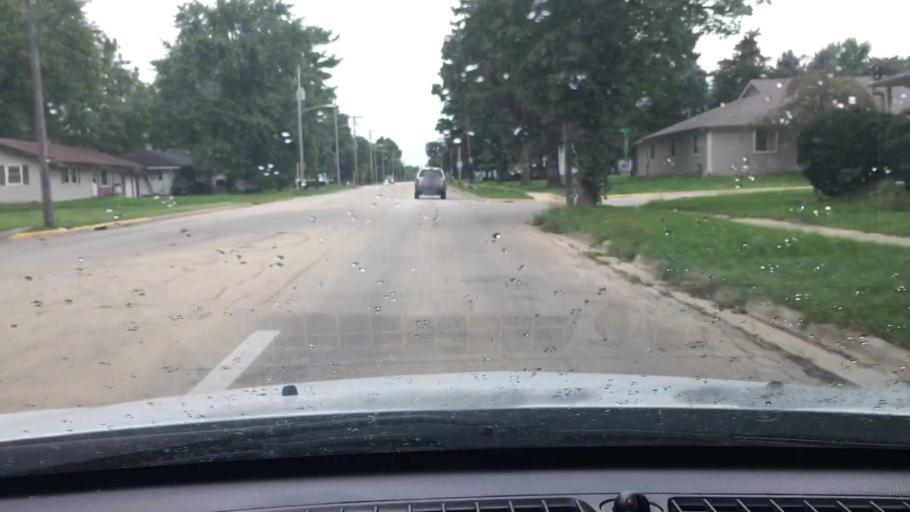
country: US
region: Illinois
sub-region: Ogle County
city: Rochelle
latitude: 41.9132
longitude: -89.0587
